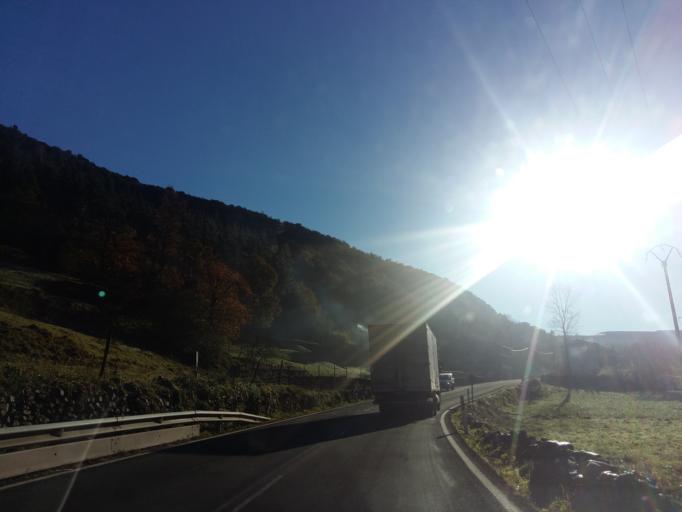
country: ES
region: Basque Country
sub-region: Bizkaia
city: Lanestosa
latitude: 43.2285
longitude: -3.4452
